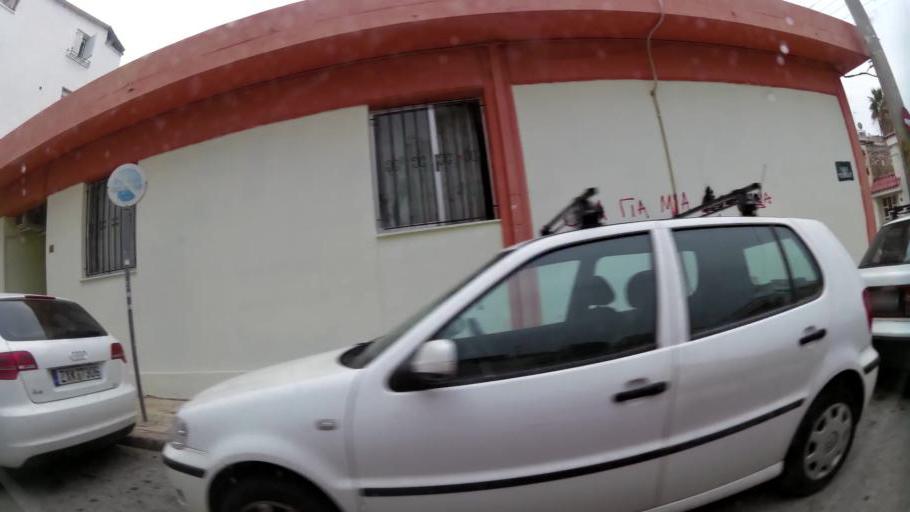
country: GR
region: Attica
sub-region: Nomarchia Athinas
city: Peristeri
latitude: 38.0088
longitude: 23.6941
